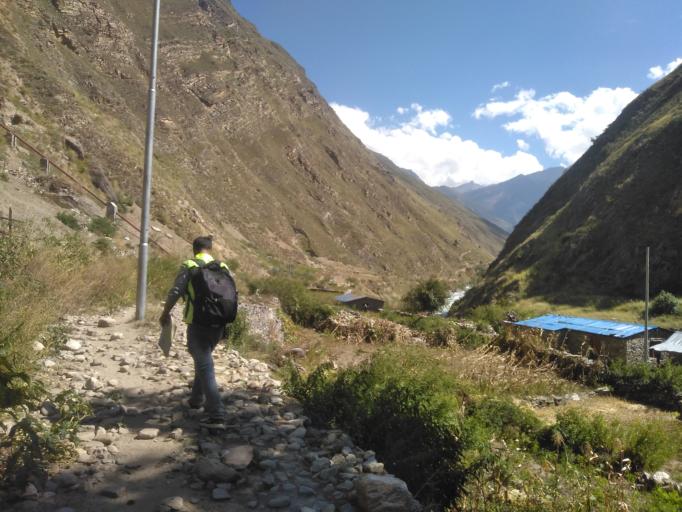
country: NP
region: Western Region
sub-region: Dhawalagiri Zone
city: Jomsom
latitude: 28.9373
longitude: 82.9575
